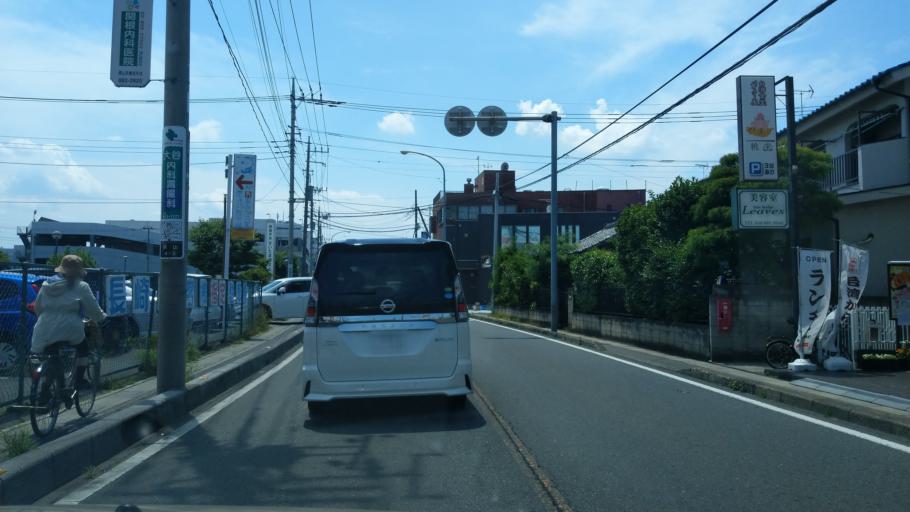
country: JP
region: Saitama
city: Saitama
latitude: 35.8713
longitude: 139.6741
